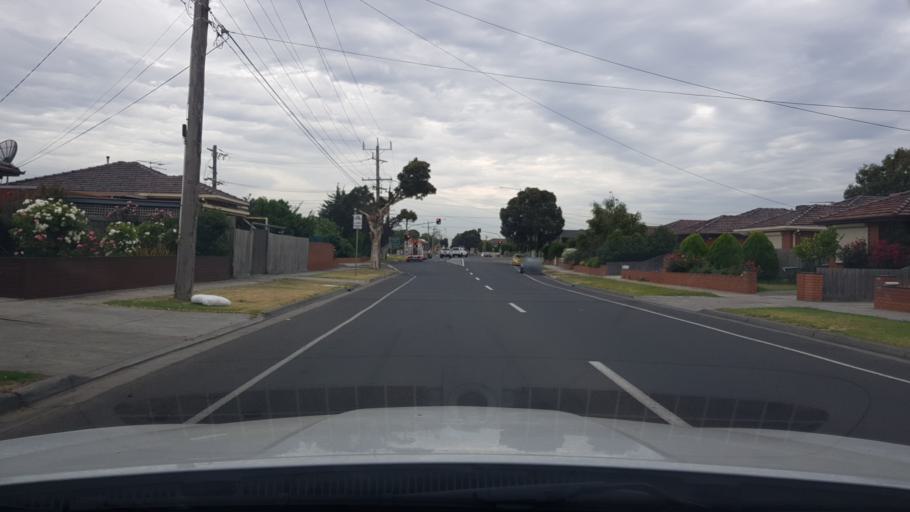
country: AU
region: Victoria
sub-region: Whittlesea
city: Lalor
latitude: -37.6640
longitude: 145.0035
